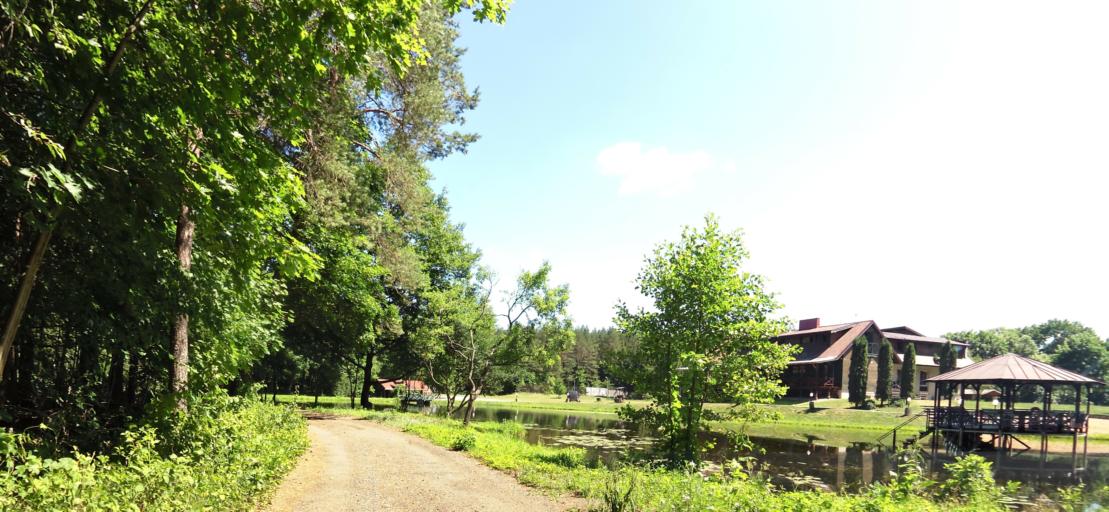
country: LT
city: Grigiskes
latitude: 54.7910
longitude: 24.9669
